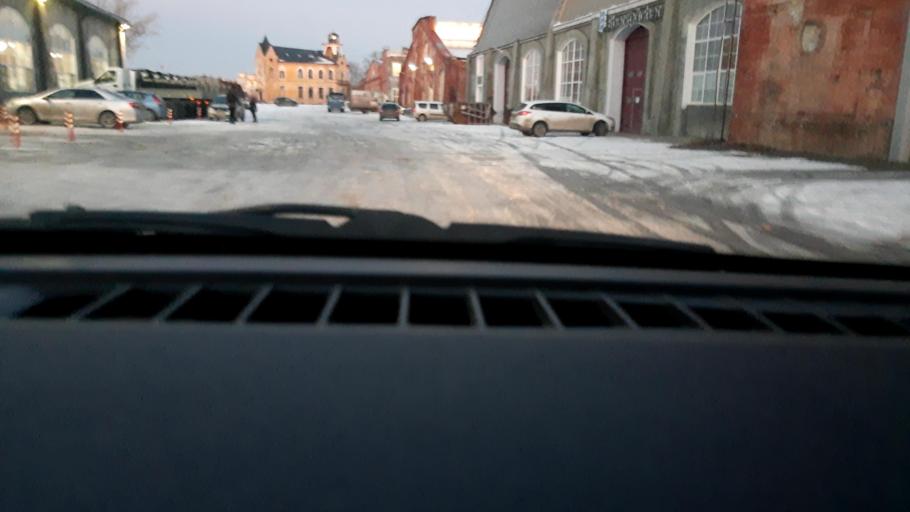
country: RU
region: Nizjnij Novgorod
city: Neklyudovo
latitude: 56.3539
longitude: 43.8743
